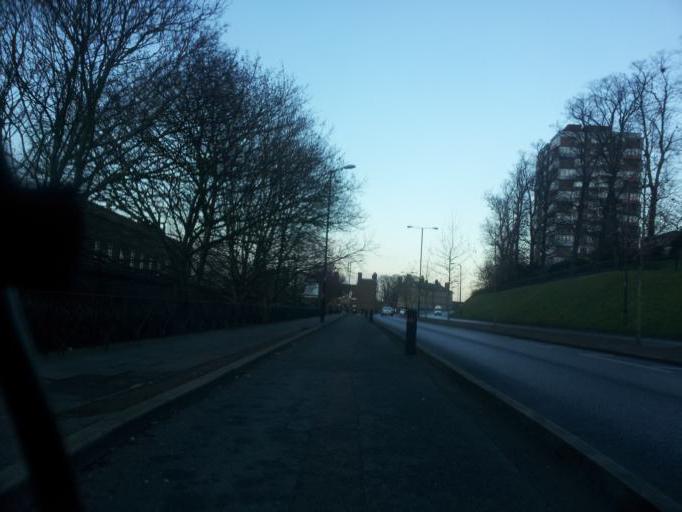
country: GB
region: England
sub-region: Kent
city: Chatham
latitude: 51.3902
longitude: 0.5259
